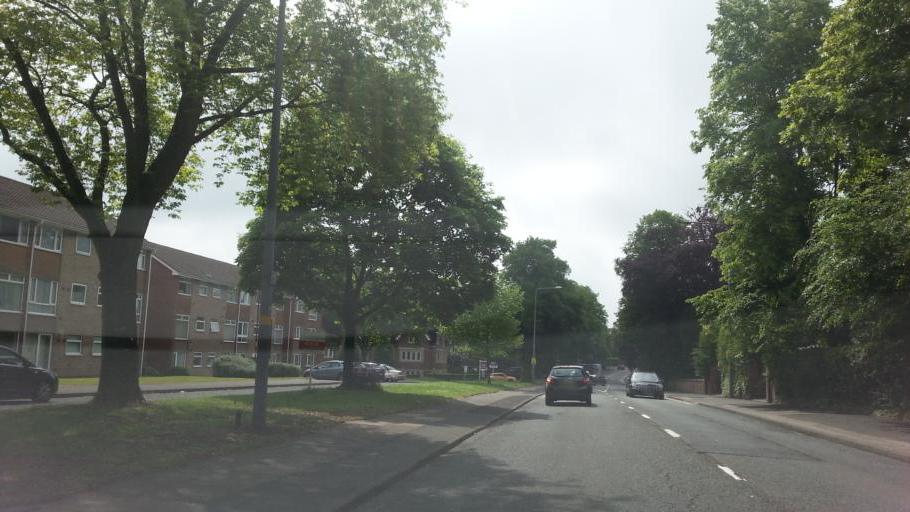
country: GB
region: England
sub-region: City and Borough of Birmingham
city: Sutton Coldfield
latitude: 52.5741
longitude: -1.8255
